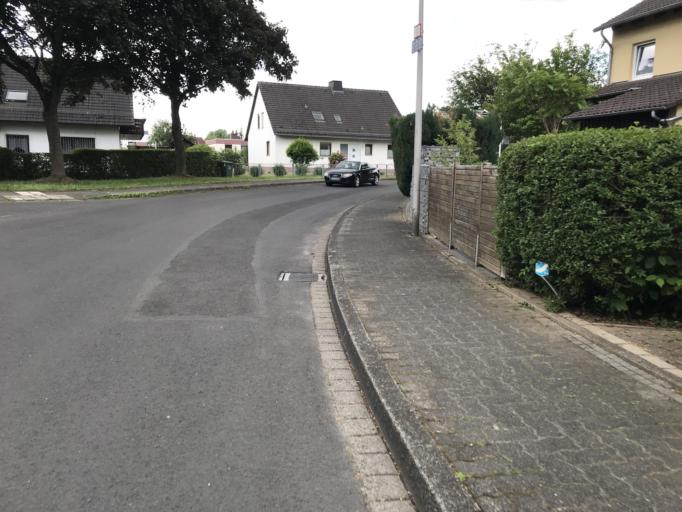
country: DE
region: Hesse
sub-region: Regierungsbezirk Kassel
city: Baunatal
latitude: 51.2546
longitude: 9.4069
